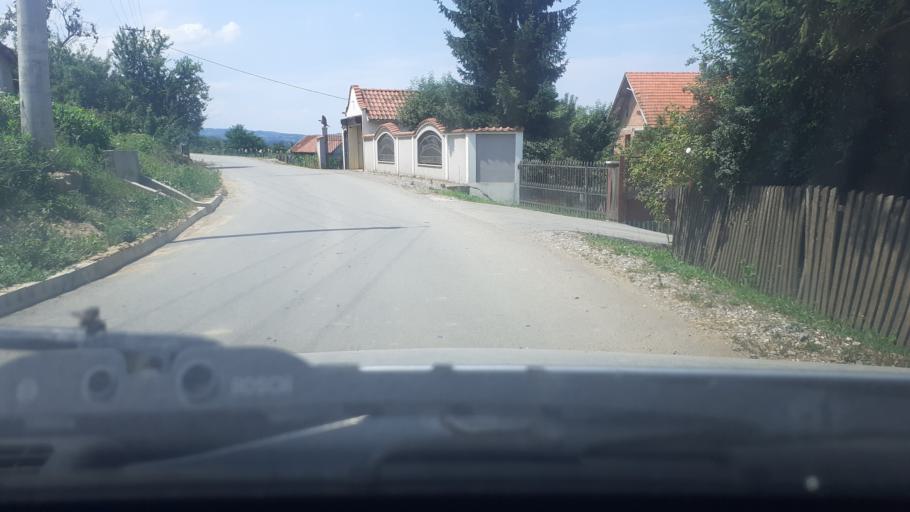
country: RS
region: Central Serbia
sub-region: Kolubarski Okrug
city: Osecina
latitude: 44.3916
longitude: 19.5001
